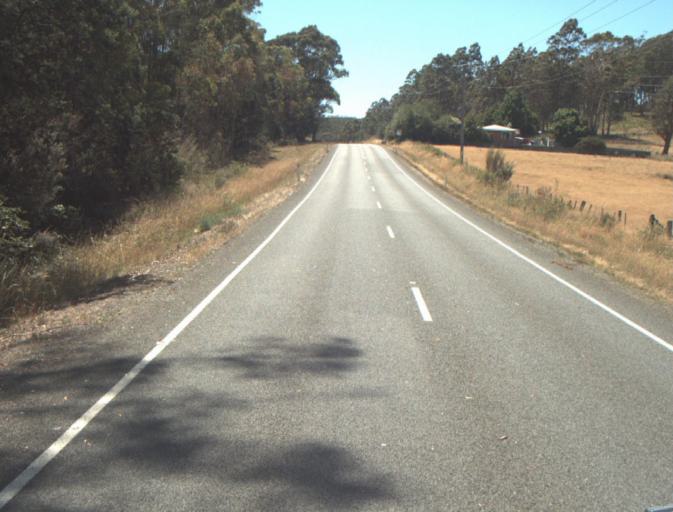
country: AU
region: Tasmania
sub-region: Launceston
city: Newstead
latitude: -41.3883
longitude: 147.3033
